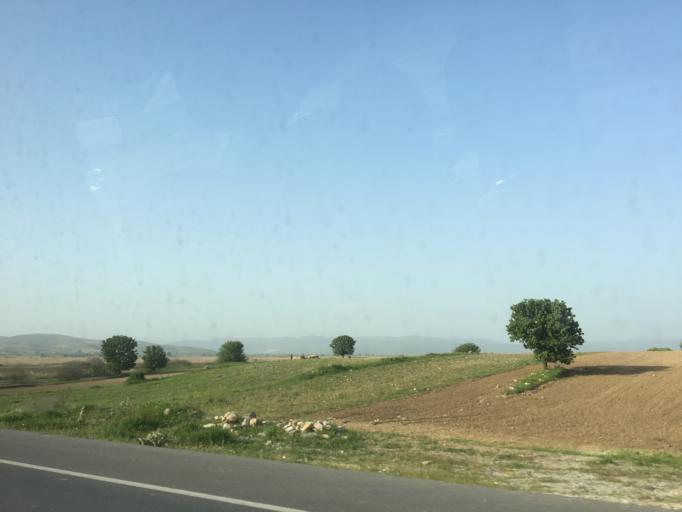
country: TR
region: Manisa
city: Golmarmara
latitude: 38.6253
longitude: 27.9348
